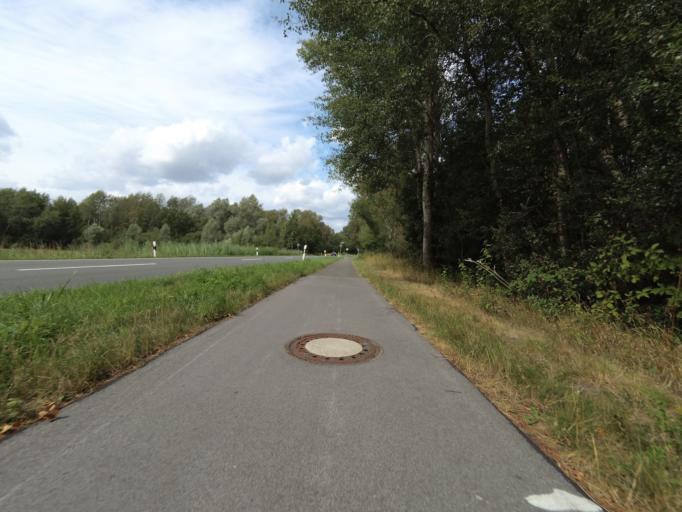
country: DE
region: North Rhine-Westphalia
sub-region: Regierungsbezirk Munster
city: Gronau
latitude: 52.1633
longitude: 6.9804
